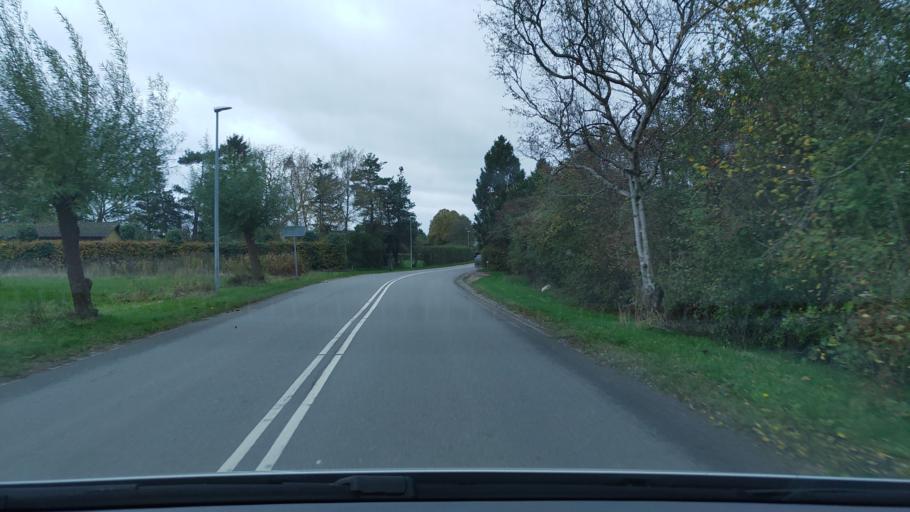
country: DK
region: Capital Region
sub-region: Tarnby Kommune
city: Tarnby
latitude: 55.6057
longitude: 12.6069
